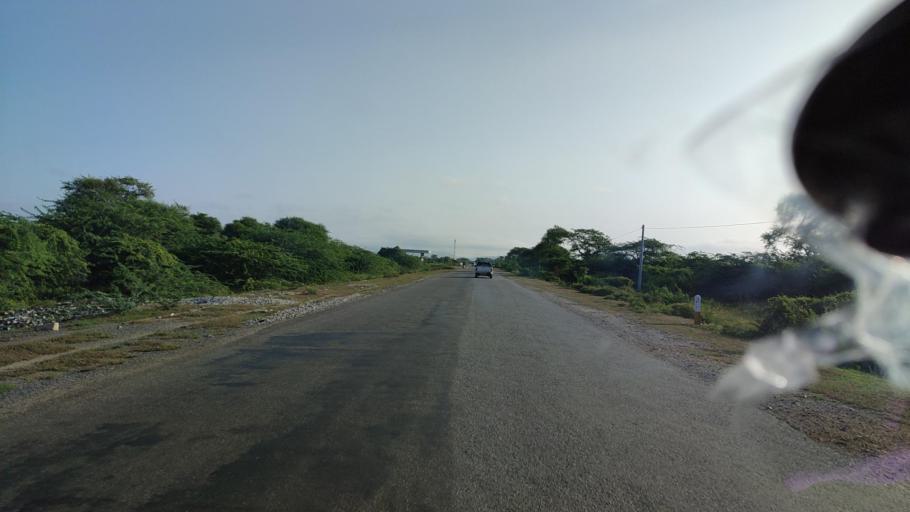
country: MM
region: Mandalay
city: Yamethin
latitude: 20.6669
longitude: 96.1276
